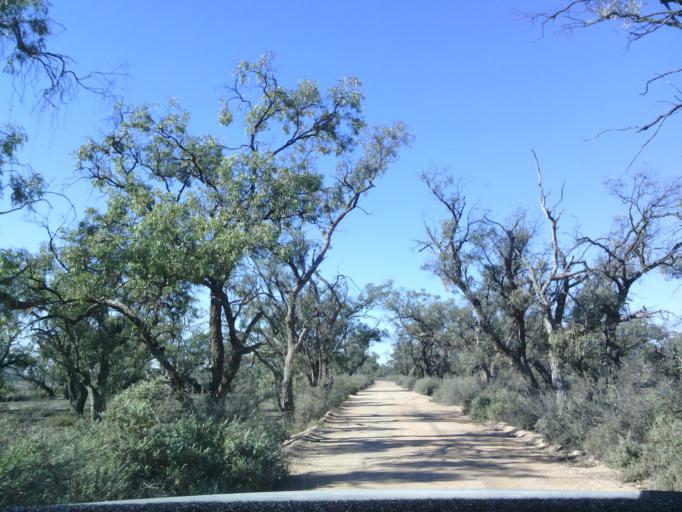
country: AU
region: South Australia
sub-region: Renmark Paringa
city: Renmark West
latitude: -34.2600
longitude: 140.6972
